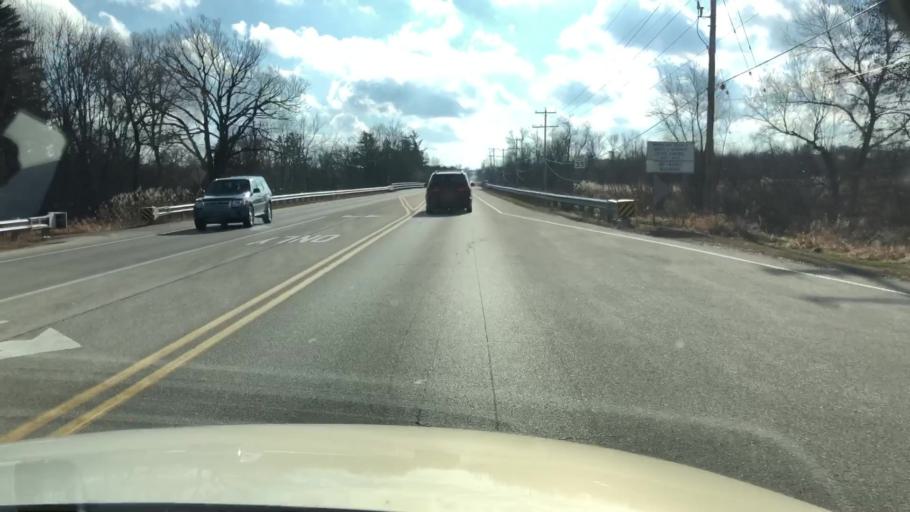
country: US
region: Wisconsin
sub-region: Waukesha County
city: Waukesha
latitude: 43.0566
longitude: -88.1859
